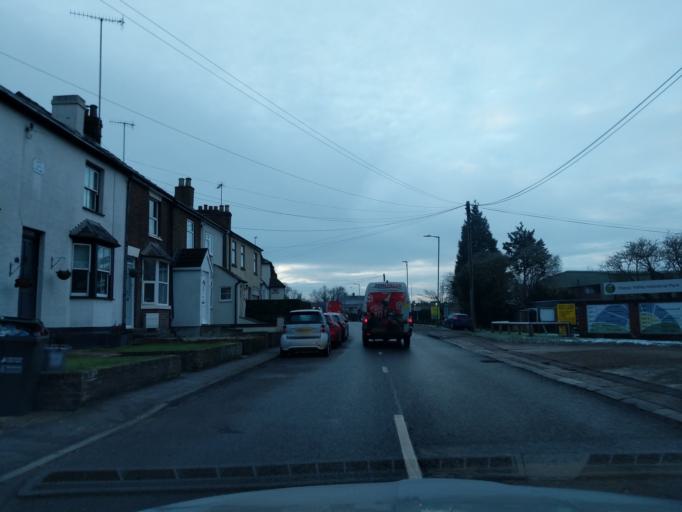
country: GB
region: England
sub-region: Hertfordshire
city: Kings Langley
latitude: 51.7161
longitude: -0.4424
